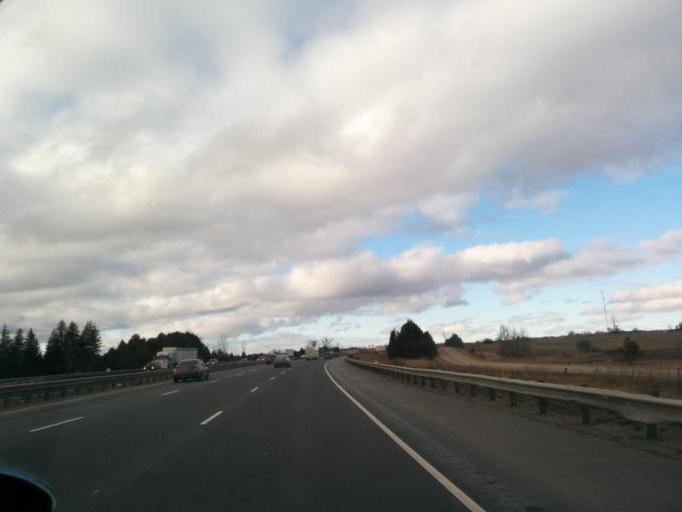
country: CA
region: Ontario
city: Bradford West Gwillimbury
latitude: 44.0659
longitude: -79.6209
